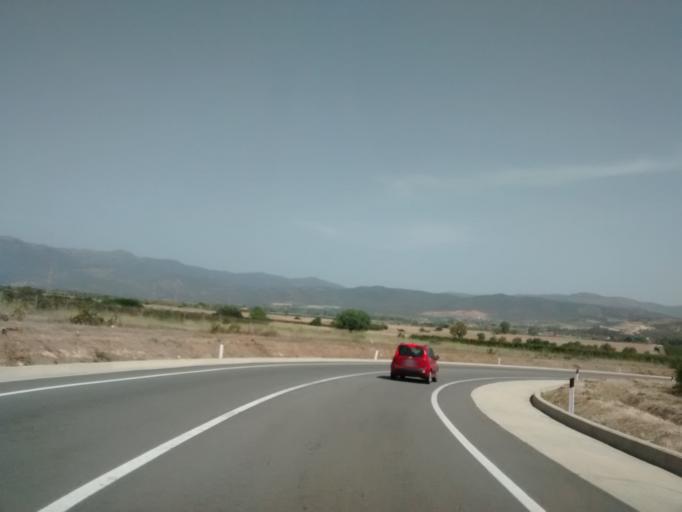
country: IT
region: Sardinia
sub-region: Provincia di Cagliari
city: Quartu Sant'Elena
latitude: 39.2601
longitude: 9.2588
